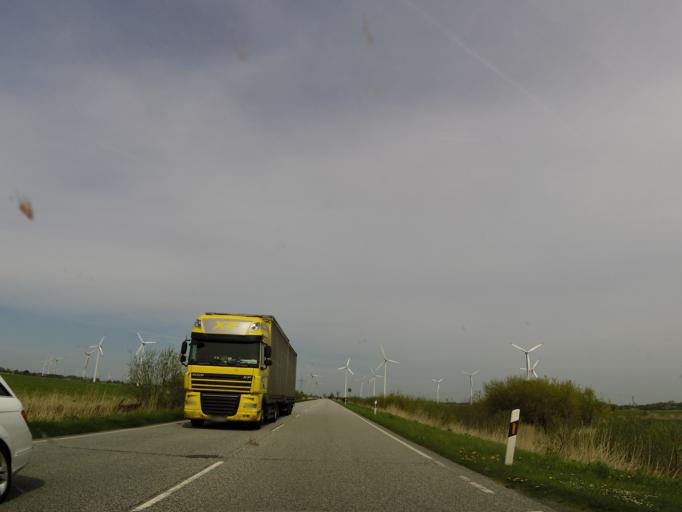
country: DE
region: Schleswig-Holstein
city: Stelle-Wittenwurth
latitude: 54.2559
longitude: 9.0366
